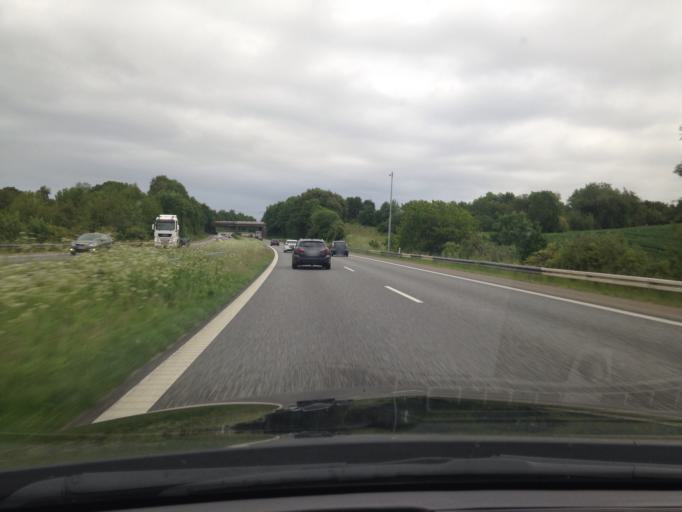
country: DK
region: South Denmark
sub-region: Fredericia Kommune
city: Taulov
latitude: 55.5425
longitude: 9.5963
